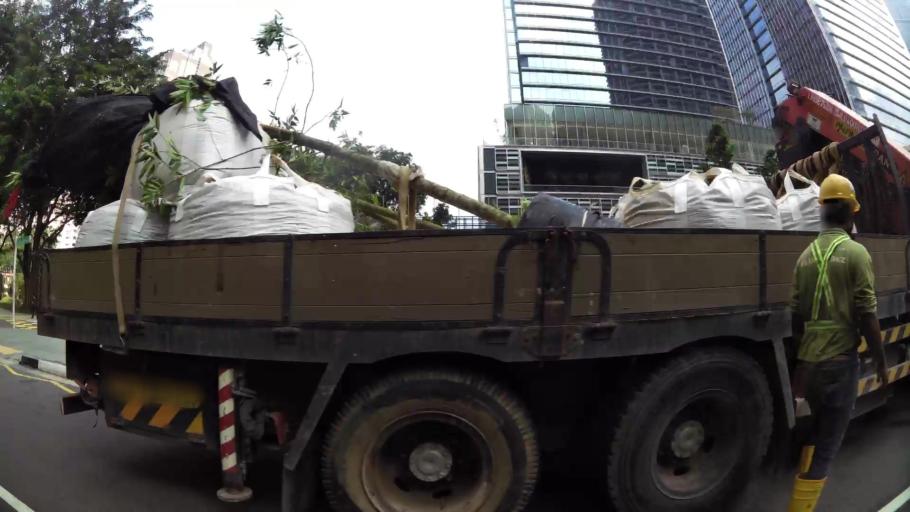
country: SG
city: Singapore
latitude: 1.2761
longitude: 103.8449
